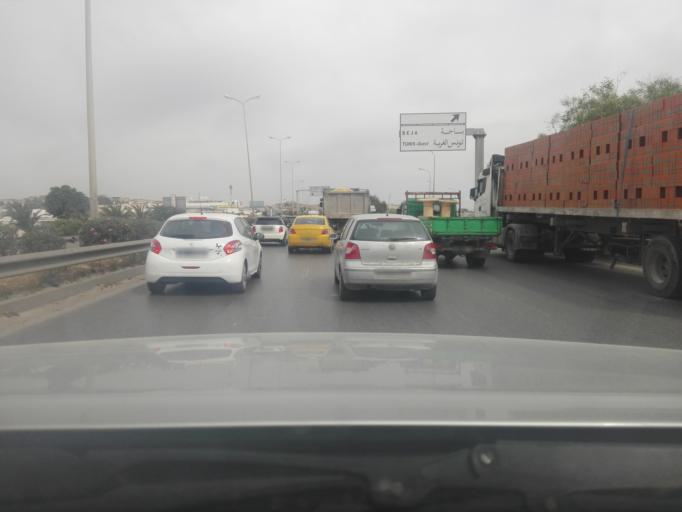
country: TN
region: Bin 'Arus
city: Ben Arous
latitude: 36.7579
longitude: 10.2005
